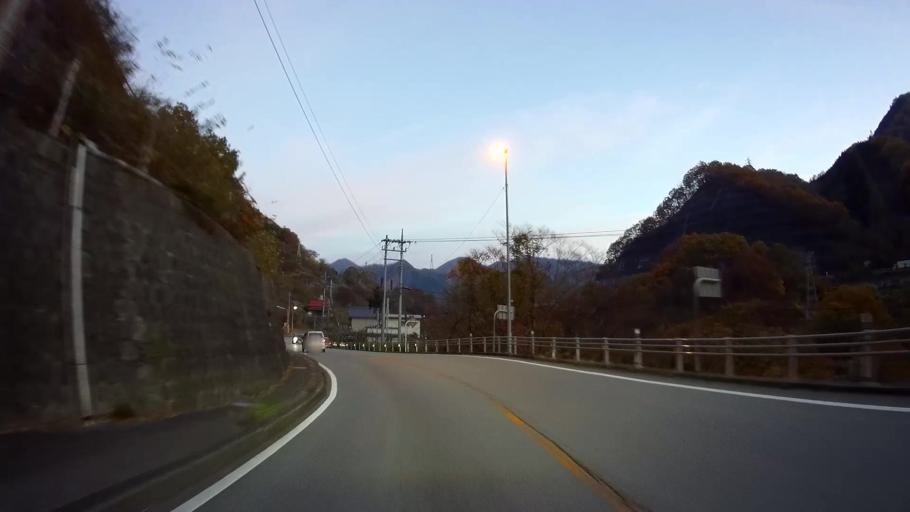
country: JP
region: Yamanashi
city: Enzan
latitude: 35.6481
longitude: 138.7621
